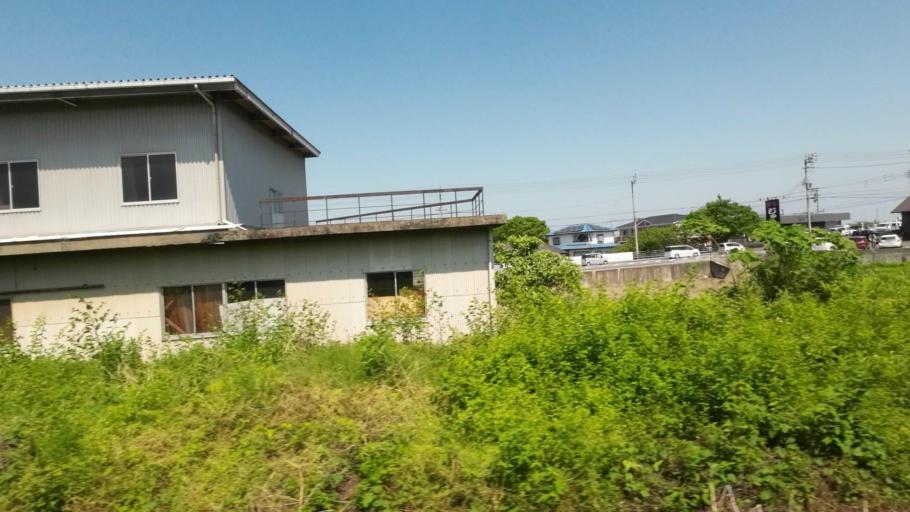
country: JP
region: Ehime
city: Niihama
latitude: 33.9534
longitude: 133.3008
